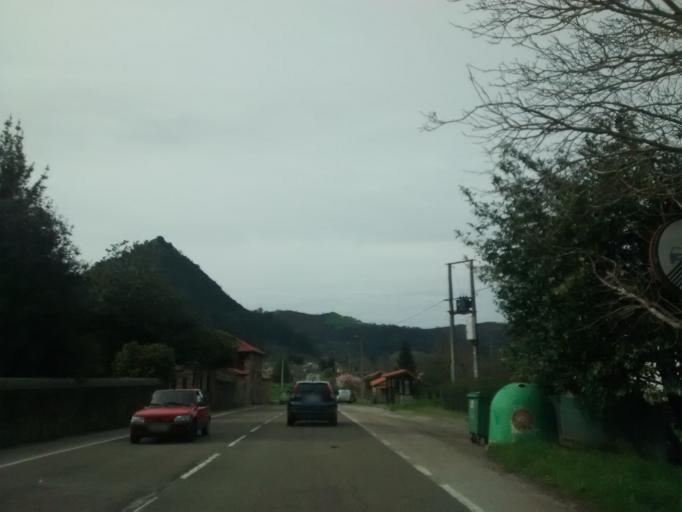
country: ES
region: Cantabria
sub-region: Provincia de Cantabria
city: Corvera
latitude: 43.2841
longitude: -3.9523
